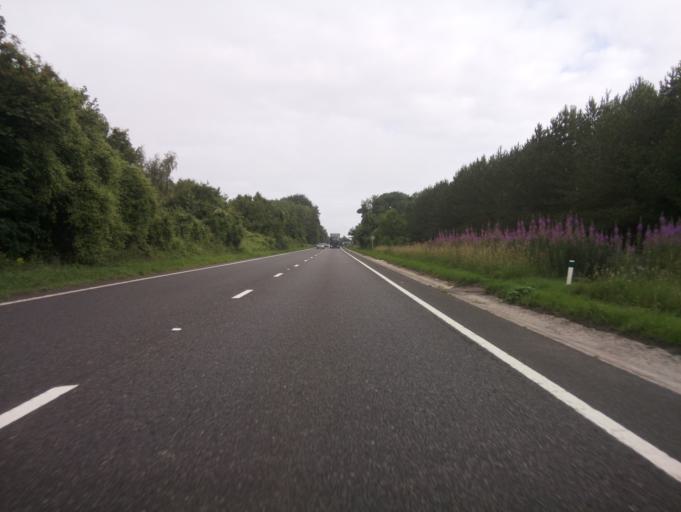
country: GB
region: England
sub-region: Gloucestershire
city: Coates
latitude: 51.7701
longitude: -2.0223
